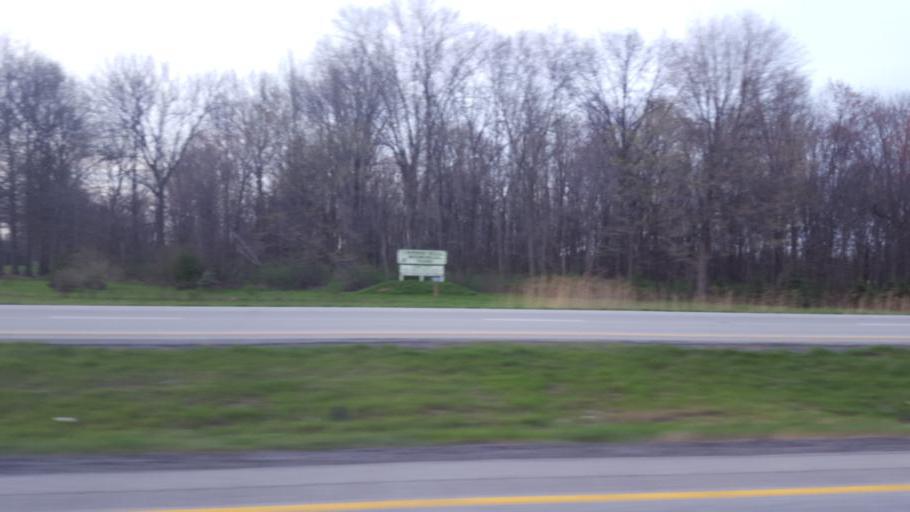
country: US
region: Ohio
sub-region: Lorain County
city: Amherst
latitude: 41.4110
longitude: -82.1846
